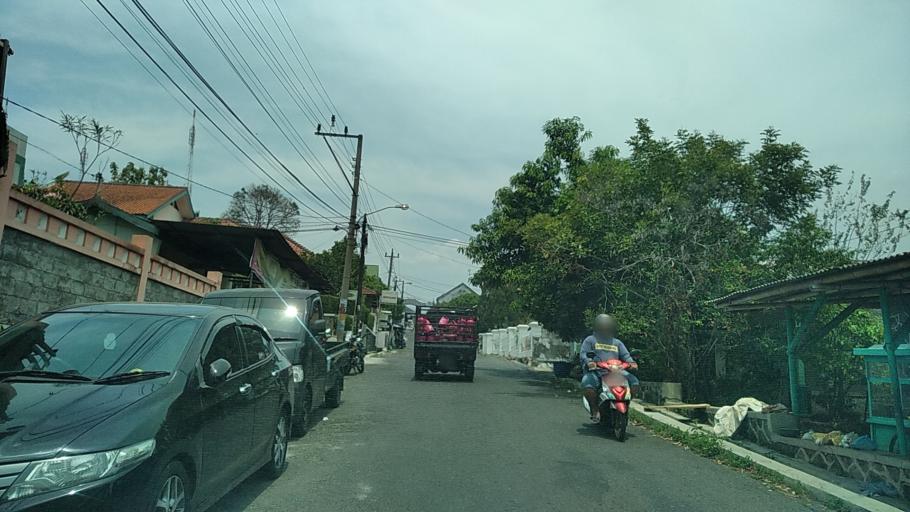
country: ID
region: Central Java
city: Semarang
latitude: -7.0448
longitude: 110.4196
